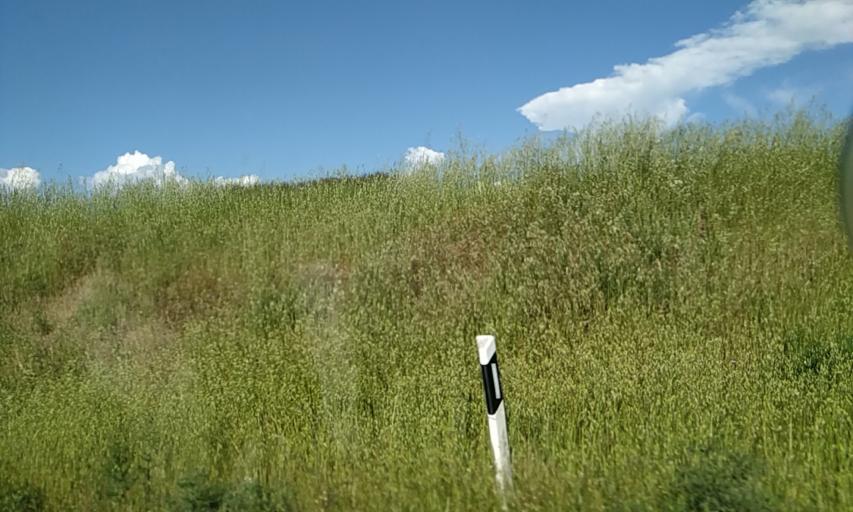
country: PT
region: Portalegre
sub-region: Portalegre
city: Urra
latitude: 39.0880
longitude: -7.4379
